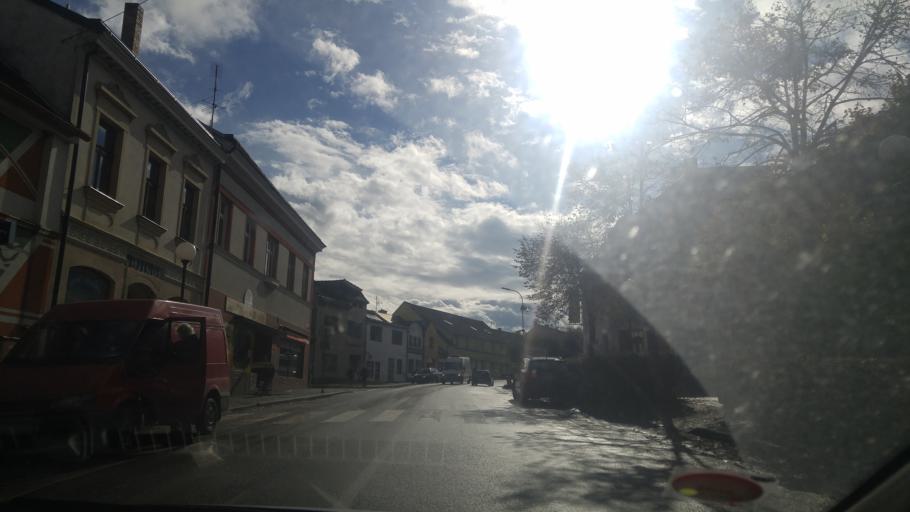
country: CZ
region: Jihocesky
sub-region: Okres Tabor
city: Veseli nad Luznici
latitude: 49.1859
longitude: 14.6991
